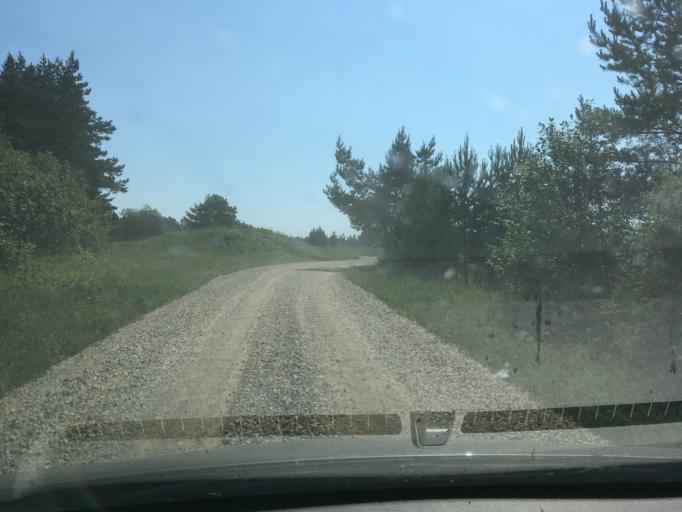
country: EE
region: Laeaene
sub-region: Lihula vald
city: Lihula
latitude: 58.5863
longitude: 23.7134
